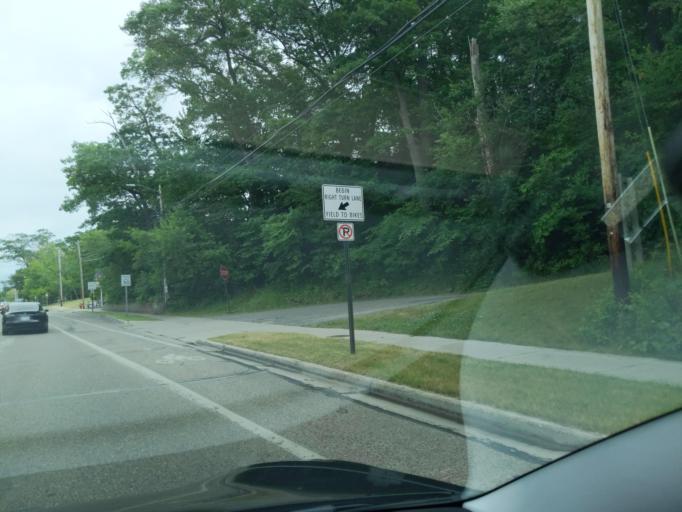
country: US
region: Michigan
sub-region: Muskegon County
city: Roosevelt Park
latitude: 43.2141
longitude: -86.3084
